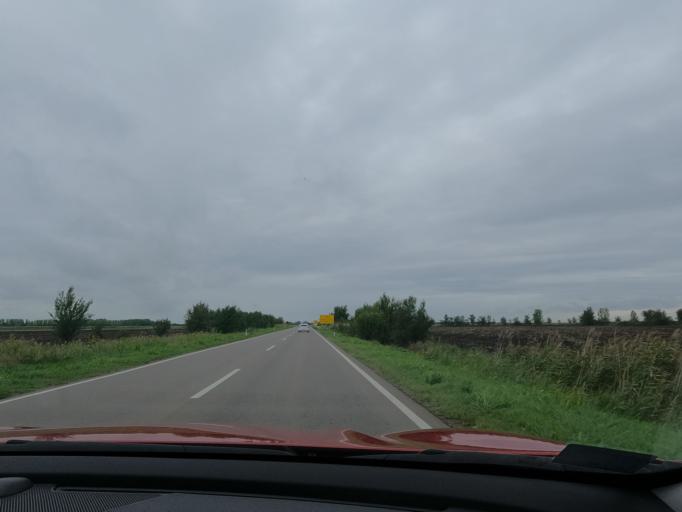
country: RS
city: Basaid
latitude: 45.6683
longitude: 20.4214
